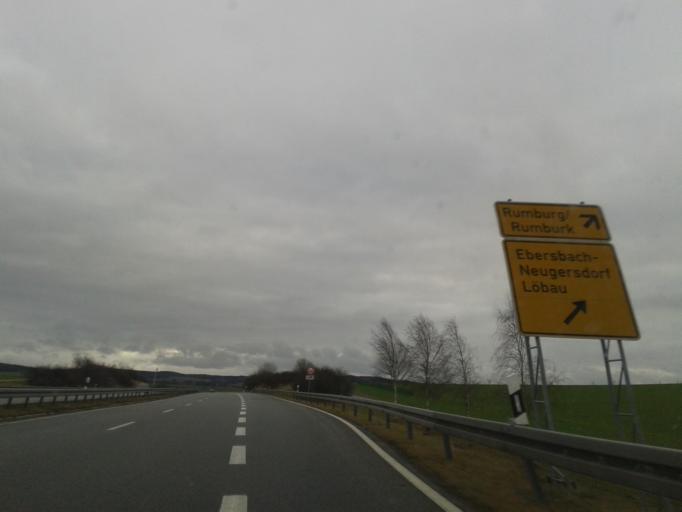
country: DE
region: Saxony
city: Grossschweidnitz
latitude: 51.0825
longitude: 14.6503
